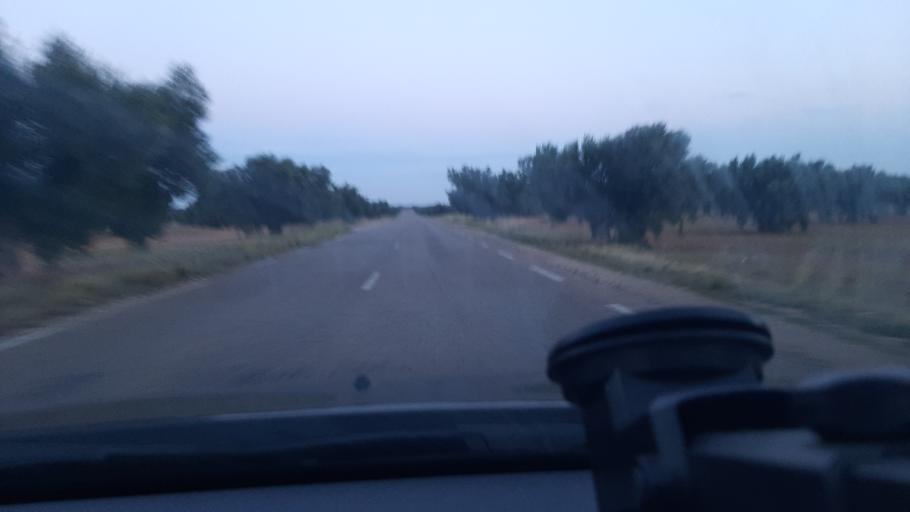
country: TN
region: Al Mahdiyah
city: Shurban
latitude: 35.0328
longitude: 10.5070
